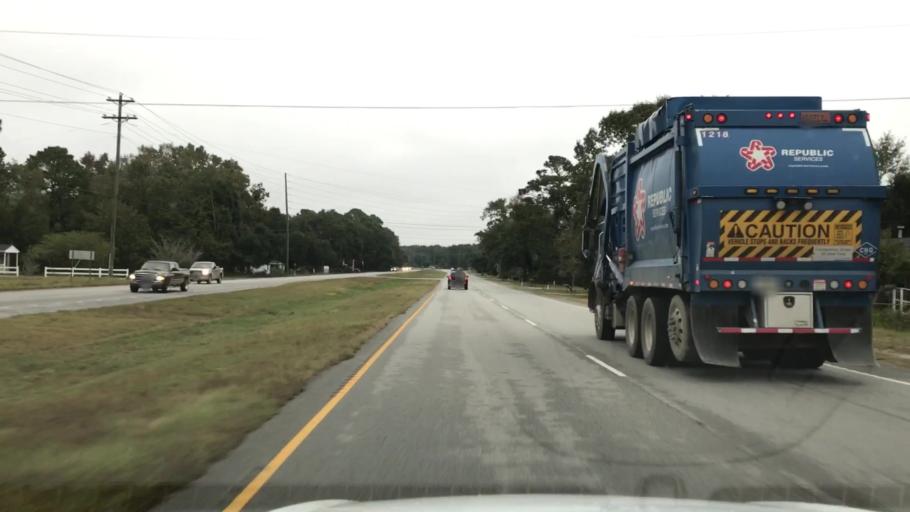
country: US
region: South Carolina
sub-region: Charleston County
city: Isle of Palms
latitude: 32.8850
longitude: -79.7481
